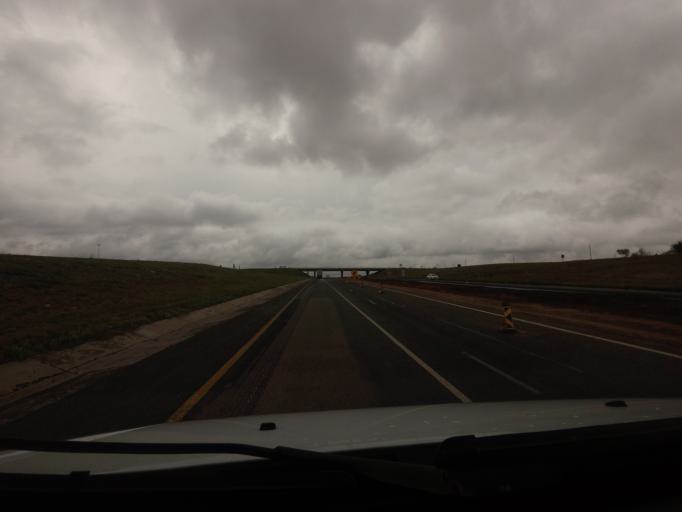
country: ZA
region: Mpumalanga
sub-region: Nkangala District Municipality
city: Witbank
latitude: -25.8739
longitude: 29.1330
